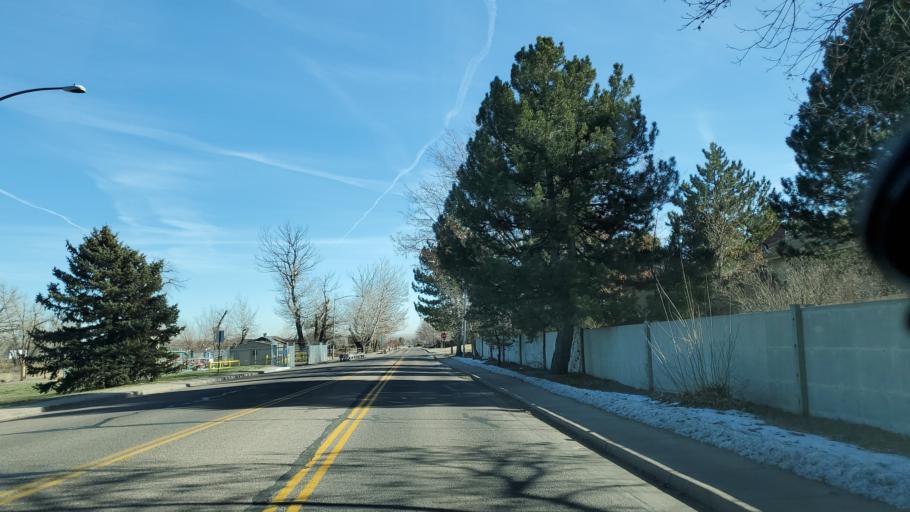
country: US
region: Colorado
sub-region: Adams County
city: Northglenn
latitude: 39.9211
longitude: -104.9510
